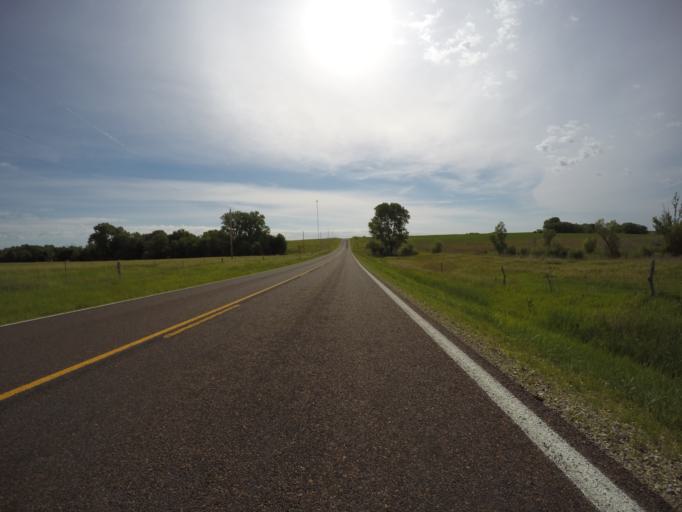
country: US
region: Kansas
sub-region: Washington County
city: Washington
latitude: 39.7119
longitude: -97.2442
